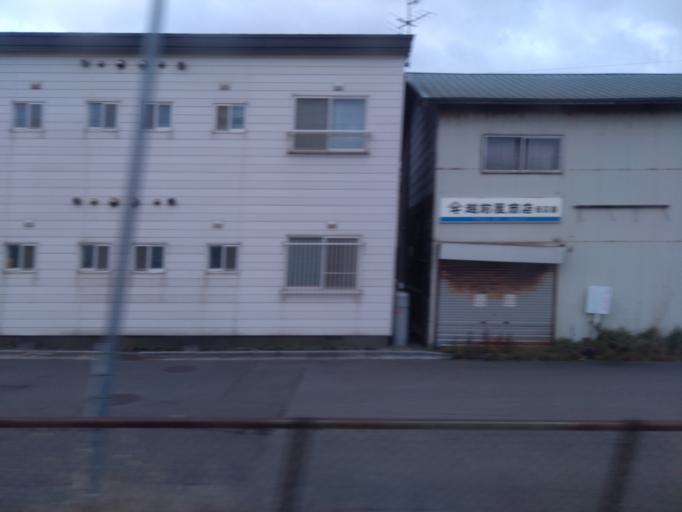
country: JP
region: Hokkaido
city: Hakodate
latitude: 41.7855
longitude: 140.7297
